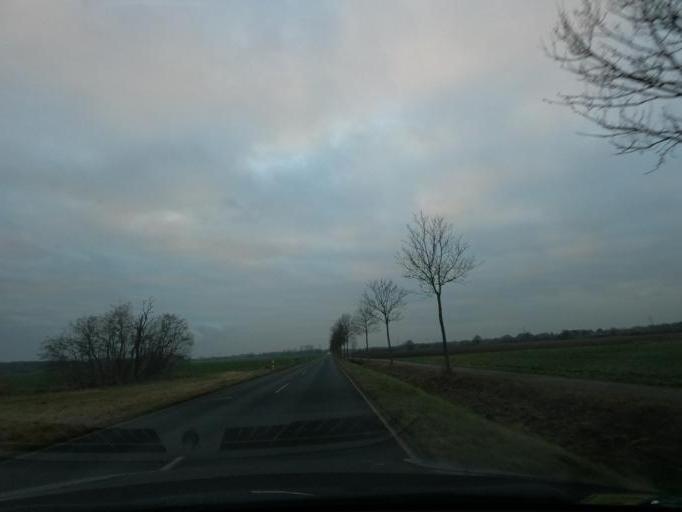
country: DE
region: Lower Saxony
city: Leiferde
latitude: 52.2184
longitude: 10.5557
